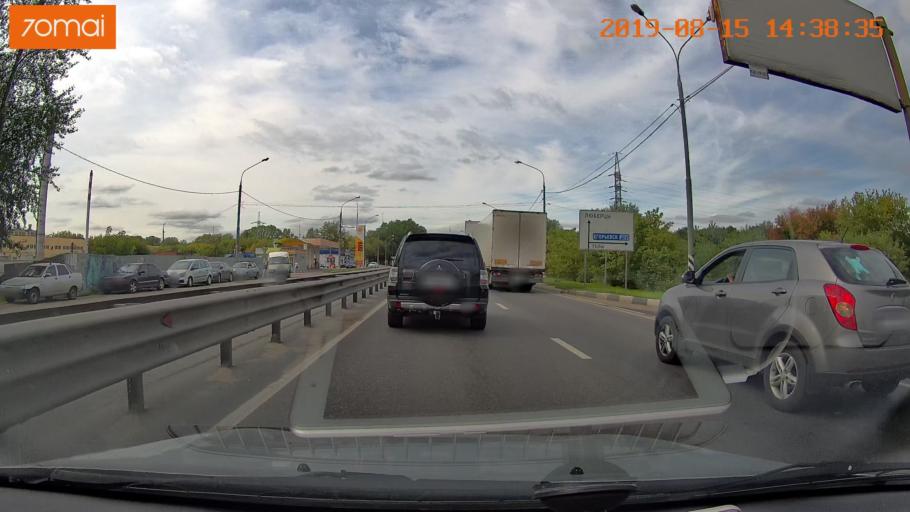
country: RU
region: Moskovskaya
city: Tomilino
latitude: 55.6566
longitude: 37.9204
